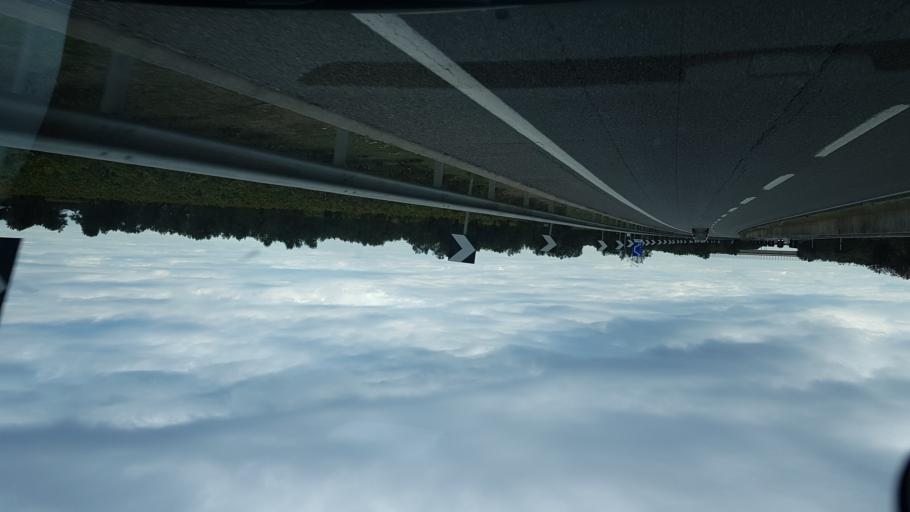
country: IT
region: Apulia
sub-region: Provincia di Brindisi
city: San Pietro Vernotico
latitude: 40.5315
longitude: 18.0100
